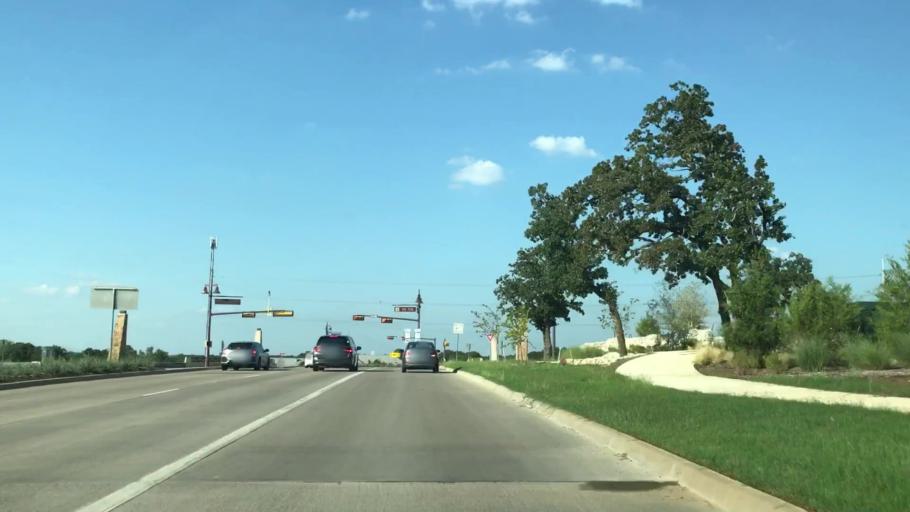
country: US
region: Texas
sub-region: Denton County
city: Trophy Club
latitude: 32.9881
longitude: -97.1819
